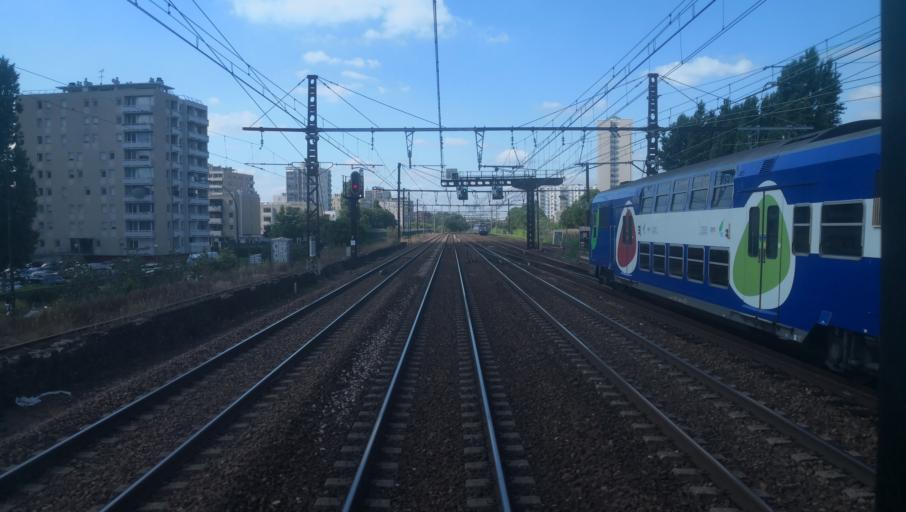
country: FR
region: Ile-de-France
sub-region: Departement du Val-de-Marne
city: Alfortville
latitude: 48.7901
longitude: 2.4314
